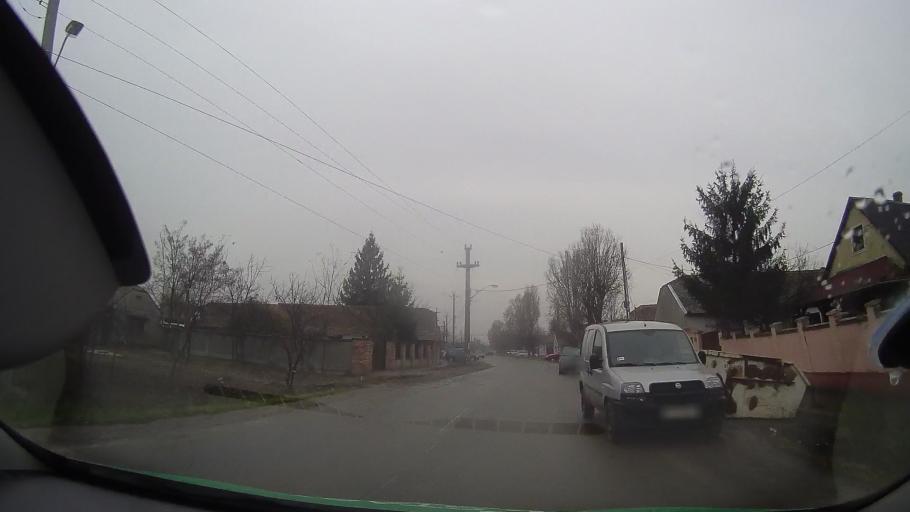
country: RO
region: Bihor
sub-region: Municipiul Salonta
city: Salonta
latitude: 46.7982
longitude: 21.6531
